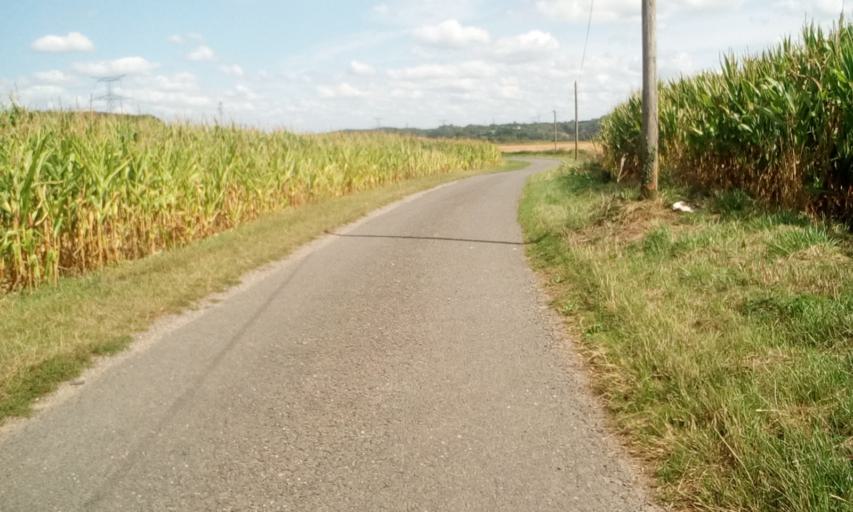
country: FR
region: Lower Normandy
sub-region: Departement du Calvados
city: Bellengreville
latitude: 49.1305
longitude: -0.1914
